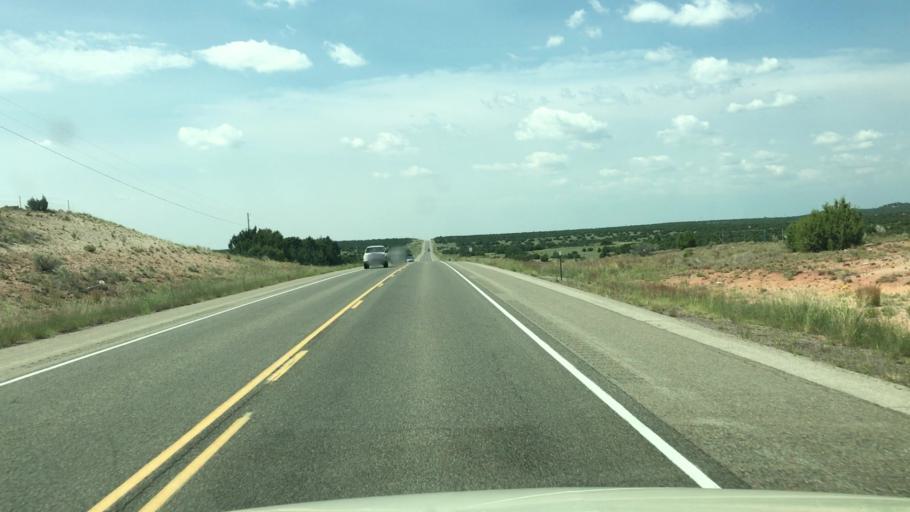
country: US
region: New Mexico
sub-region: Torrance County
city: Moriarty
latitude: 35.0448
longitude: -105.6846
